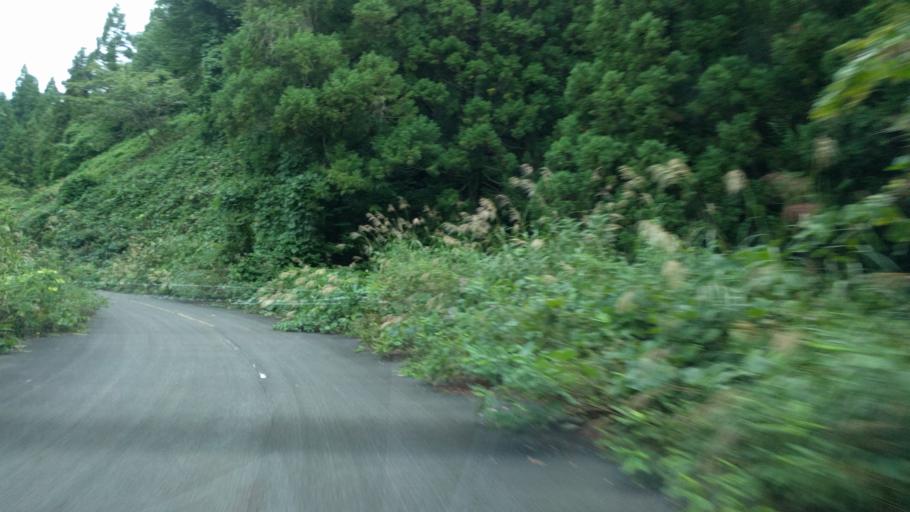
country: JP
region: Fukushima
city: Kitakata
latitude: 37.4559
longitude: 139.7790
